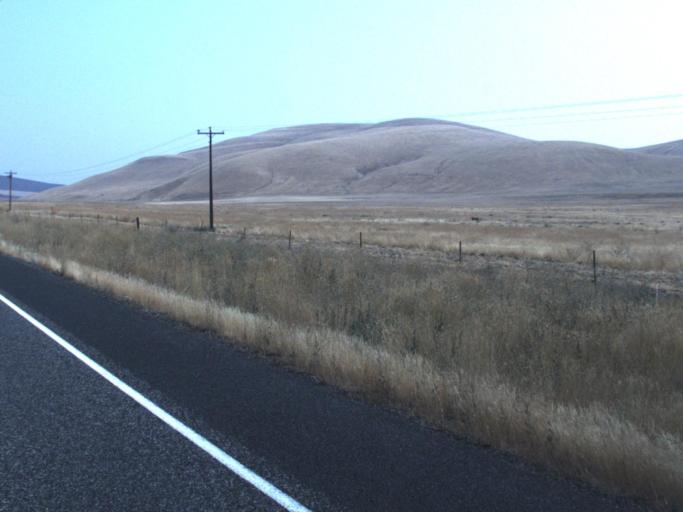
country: US
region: Washington
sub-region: Grant County
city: Desert Aire
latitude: 46.5265
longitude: -119.9452
